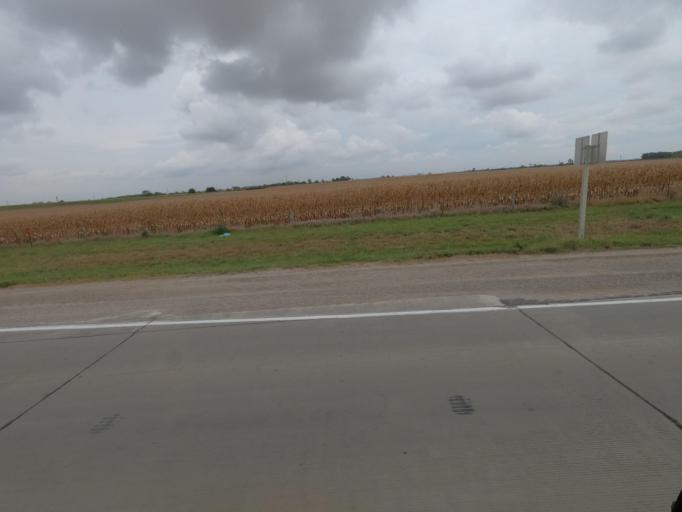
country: US
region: Iowa
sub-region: Wapello County
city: Ottumwa
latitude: 40.9958
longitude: -92.2369
